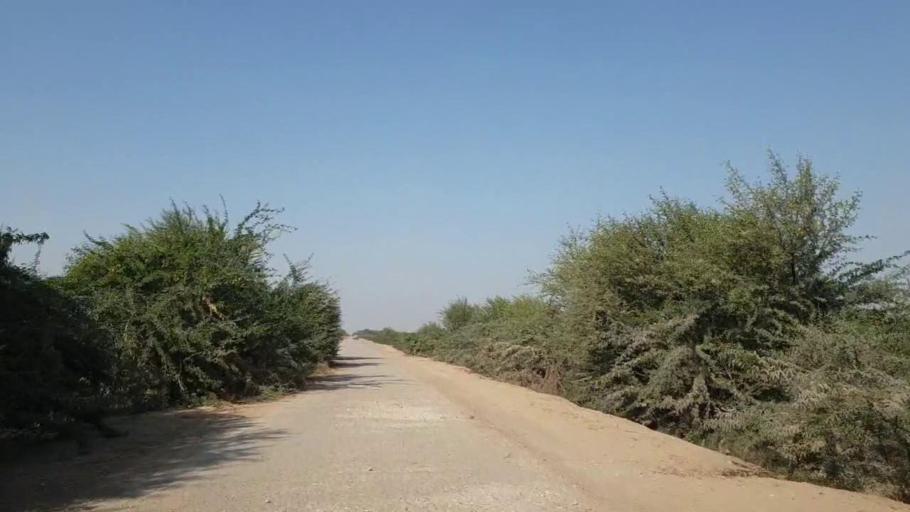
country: PK
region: Sindh
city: Digri
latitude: 24.9862
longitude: 69.1097
